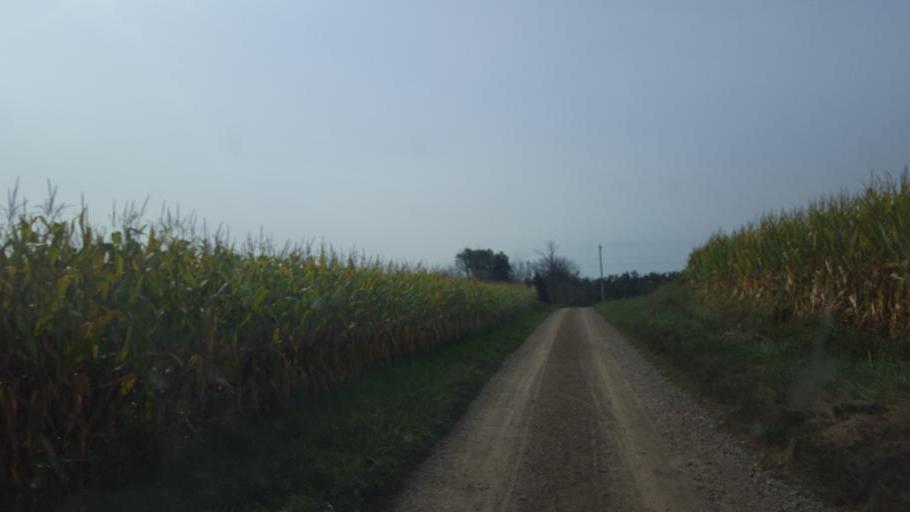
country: US
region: Ohio
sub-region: Knox County
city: Fredericktown
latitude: 40.4961
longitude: -82.5965
